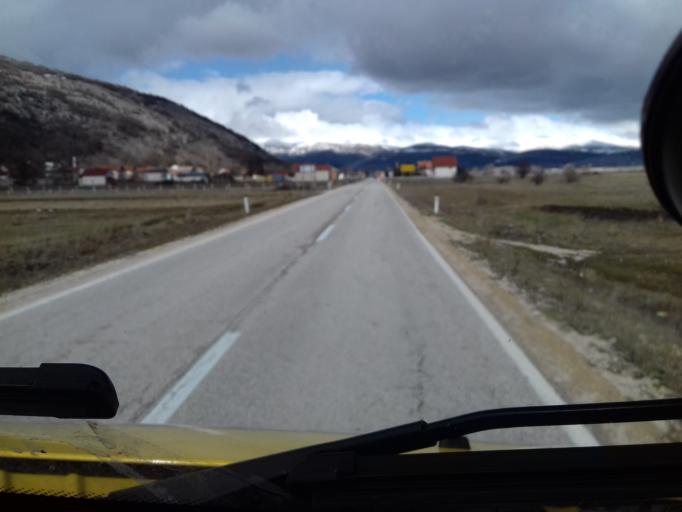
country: BA
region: Federation of Bosnia and Herzegovina
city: Tomislavgrad
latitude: 43.6560
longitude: 17.2152
